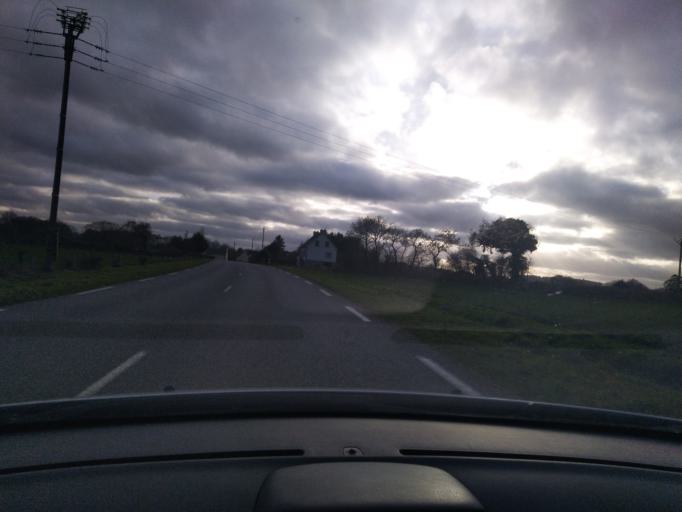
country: FR
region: Brittany
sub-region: Departement des Cotes-d'Armor
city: Plouaret
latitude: 48.5986
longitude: -3.4914
